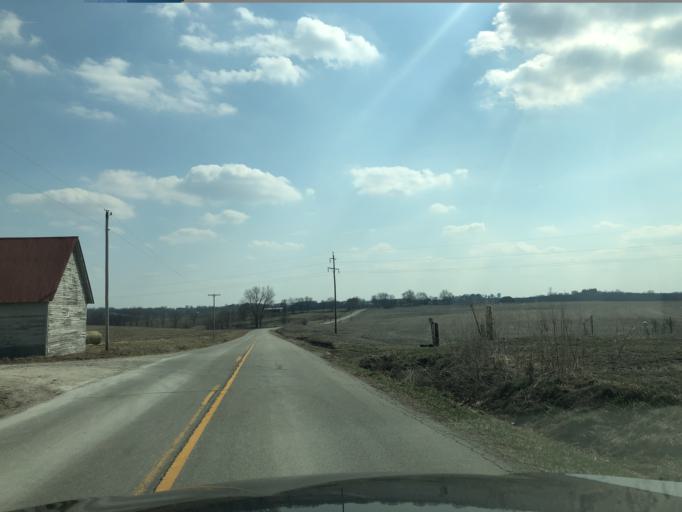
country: US
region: Missouri
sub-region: Platte County
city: Weston
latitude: 39.4620
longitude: -94.8453
